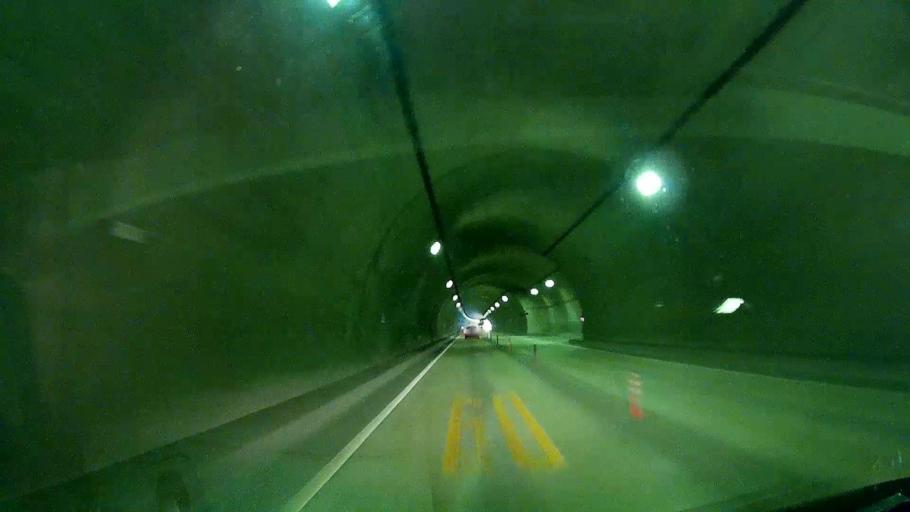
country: JP
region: Shizuoka
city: Shizuoka-shi
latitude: 35.0254
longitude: 138.3831
